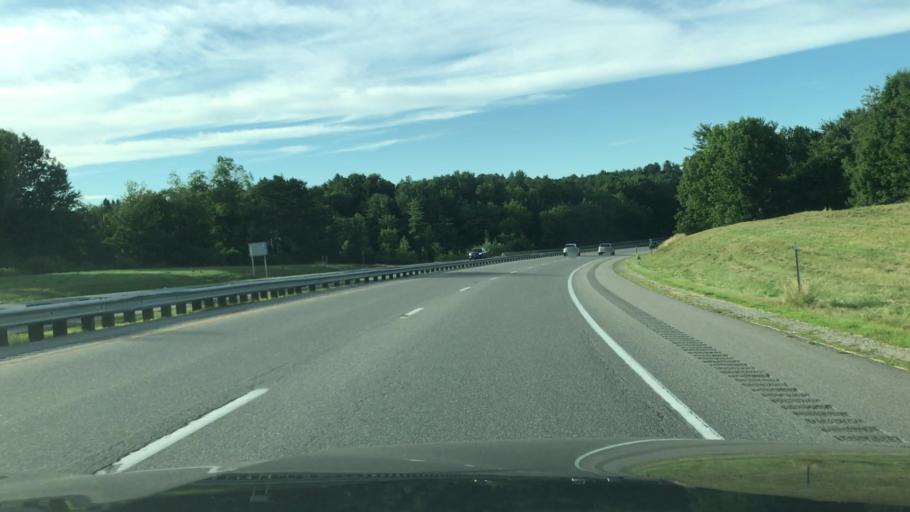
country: US
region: New Hampshire
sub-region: Strafford County
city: Dover
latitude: 43.2027
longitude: -70.8978
